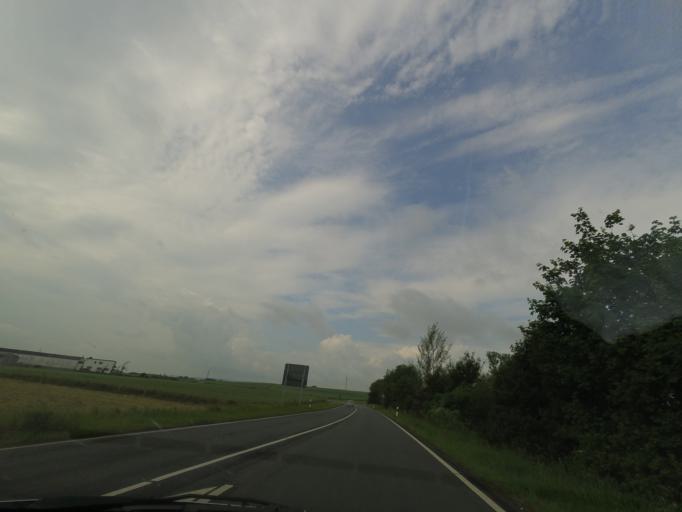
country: DE
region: Hesse
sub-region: Regierungsbezirk Giessen
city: Fronhausen
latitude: 50.7591
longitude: 8.7253
